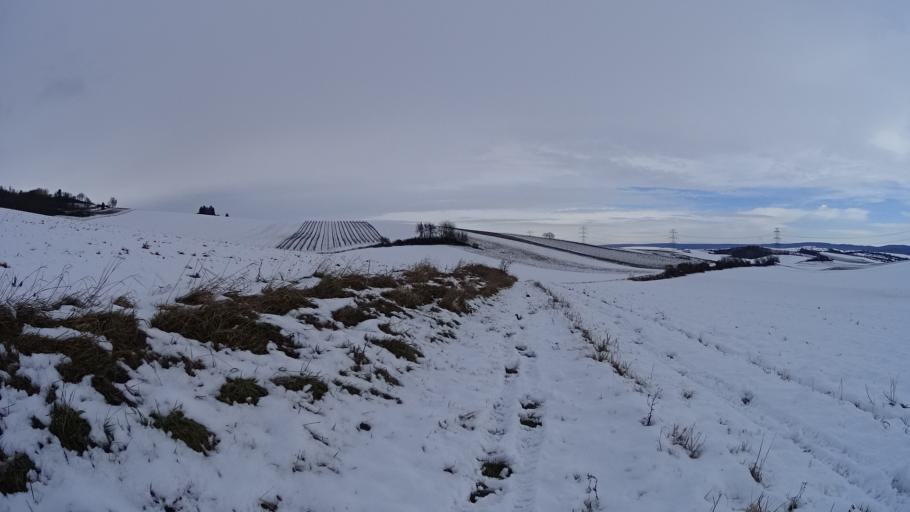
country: AT
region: Lower Austria
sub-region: Politischer Bezirk Korneuburg
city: Leobendorf
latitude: 48.3999
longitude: 16.3361
